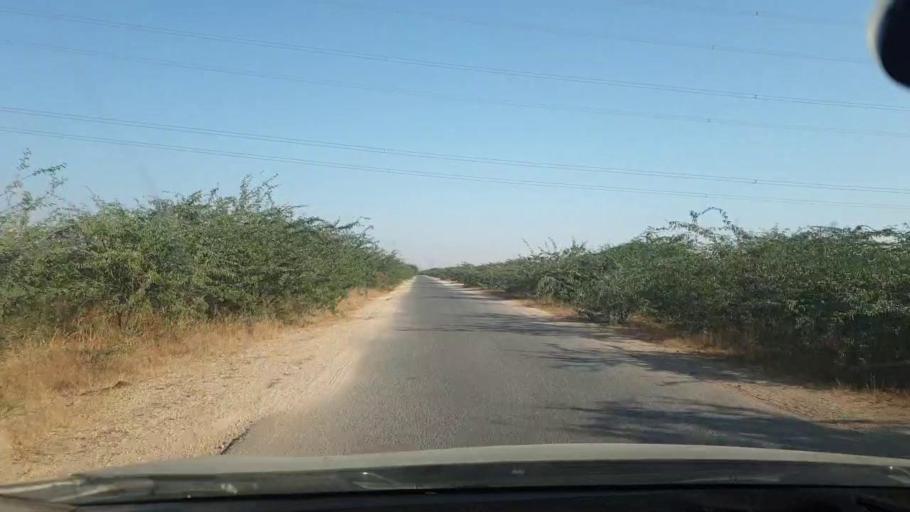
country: PK
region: Sindh
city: Malir Cantonment
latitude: 25.1613
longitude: 67.1945
